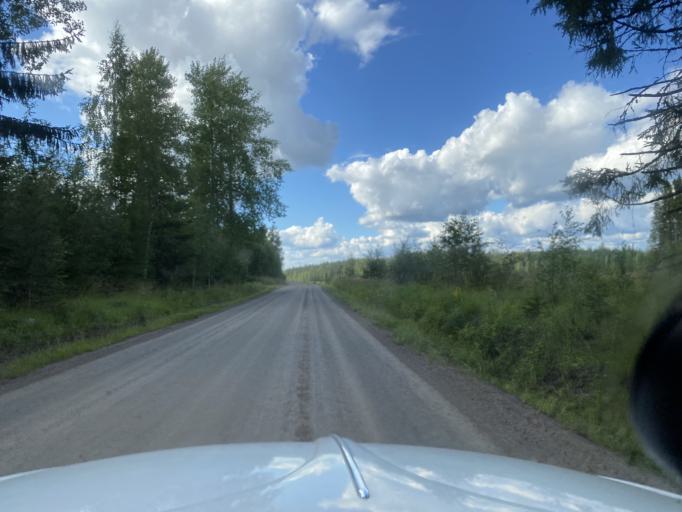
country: FI
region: Pirkanmaa
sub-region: Lounais-Pirkanmaa
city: Punkalaidun
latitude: 61.1202
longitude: 23.2684
